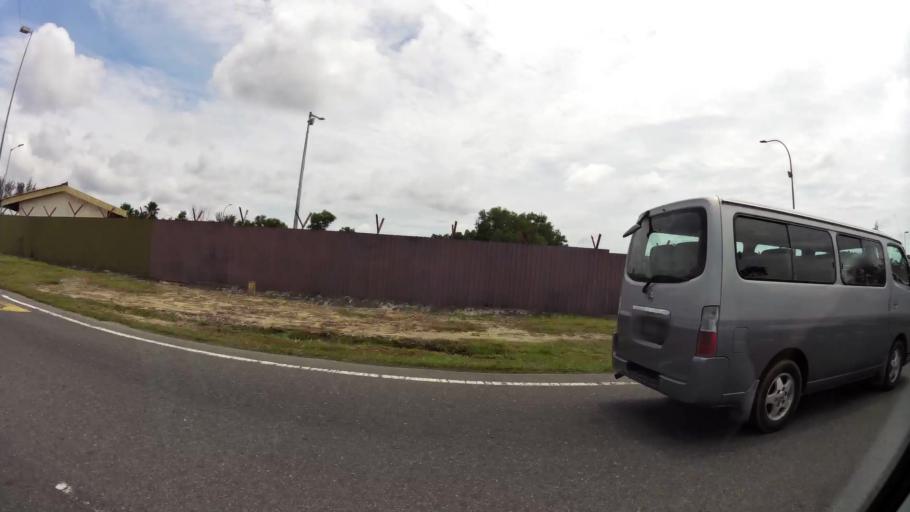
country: BN
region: Brunei and Muara
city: Bandar Seri Begawan
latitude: 4.9068
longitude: 114.9102
